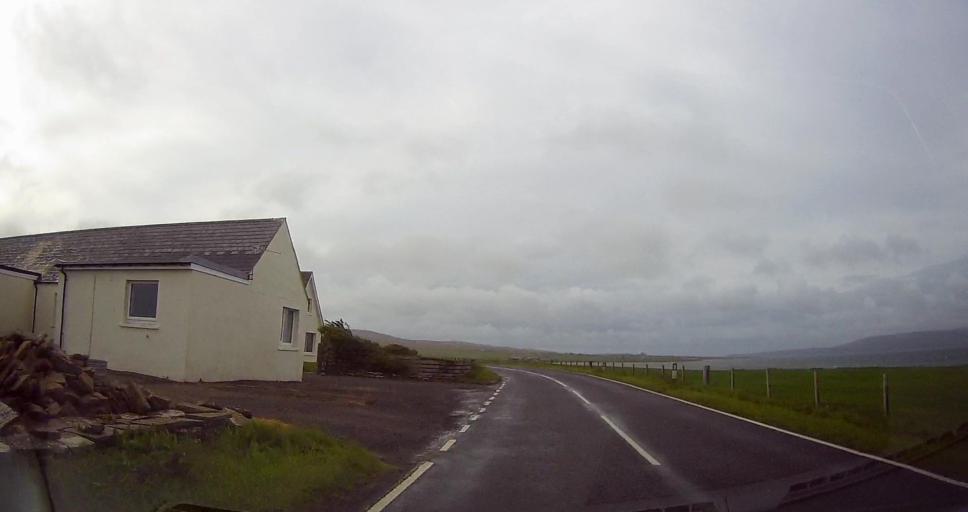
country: GB
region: Scotland
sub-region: Orkney Islands
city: Stromness
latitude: 58.9738
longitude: -3.2389
